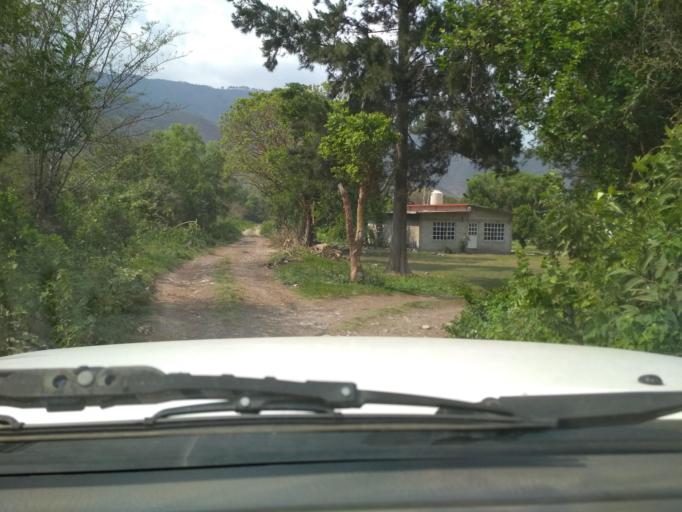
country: MX
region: Veracruz
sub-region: Acultzingo
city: Sierra de Agua
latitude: 18.7585
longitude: -97.2333
